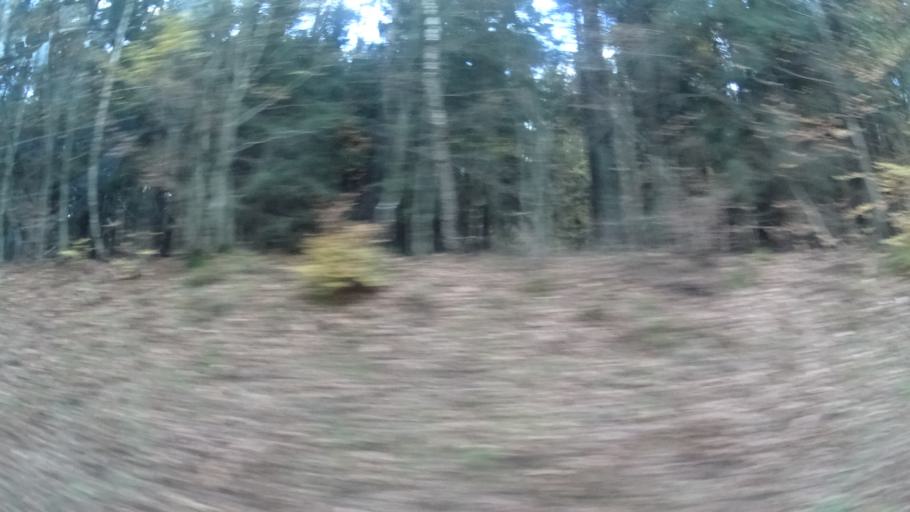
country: DE
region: Hesse
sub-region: Regierungsbezirk Kassel
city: Flieden
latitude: 50.4618
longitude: 9.5302
